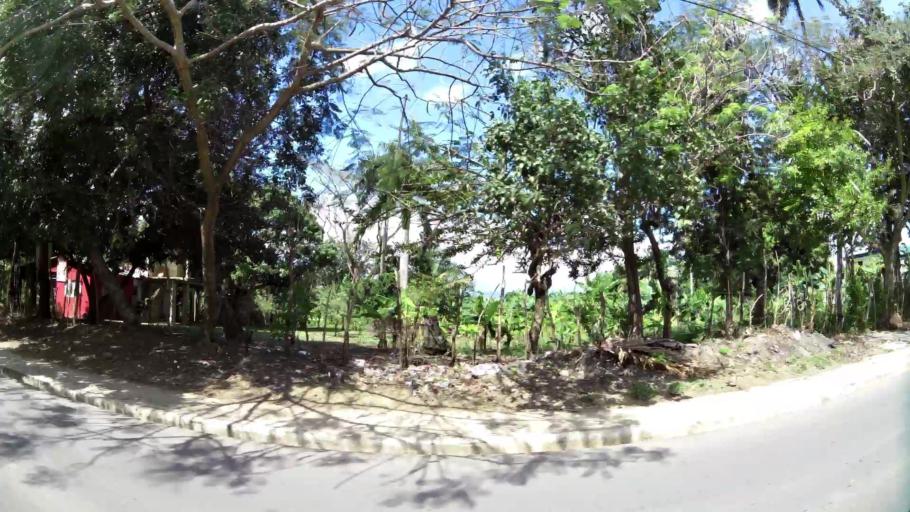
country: DO
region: Santiago
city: Licey al Medio
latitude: 19.3877
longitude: -70.6330
